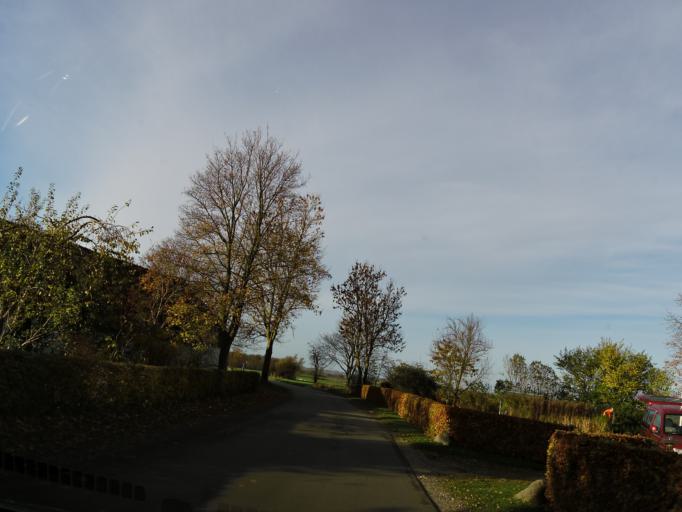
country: DK
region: Central Jutland
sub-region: Odder Kommune
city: Odder
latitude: 55.9554
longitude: 10.2401
